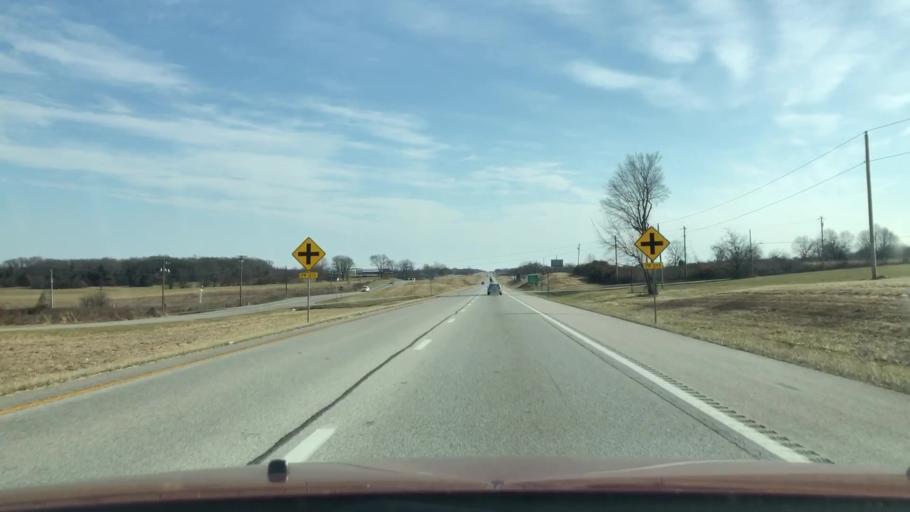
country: US
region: Missouri
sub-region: Webster County
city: Rogersville
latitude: 37.1194
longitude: -93.1575
